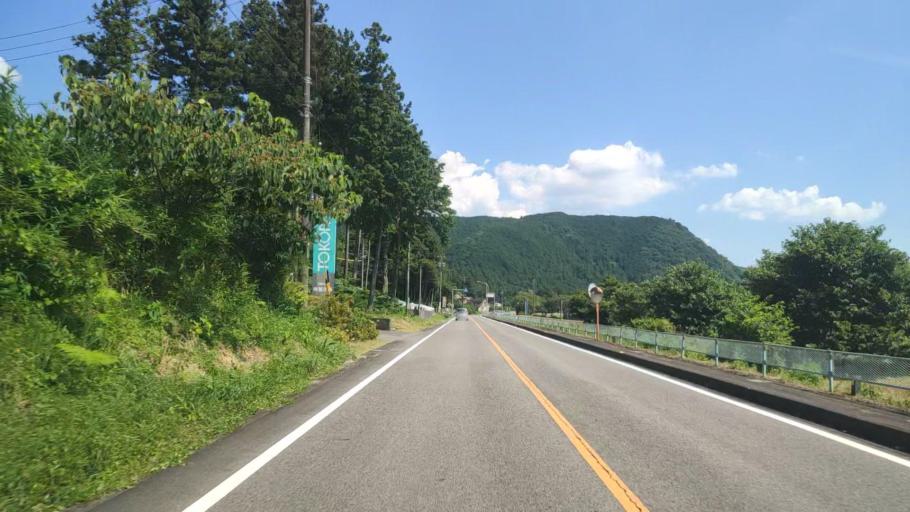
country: JP
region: Gifu
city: Godo
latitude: 35.5379
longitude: 136.6484
